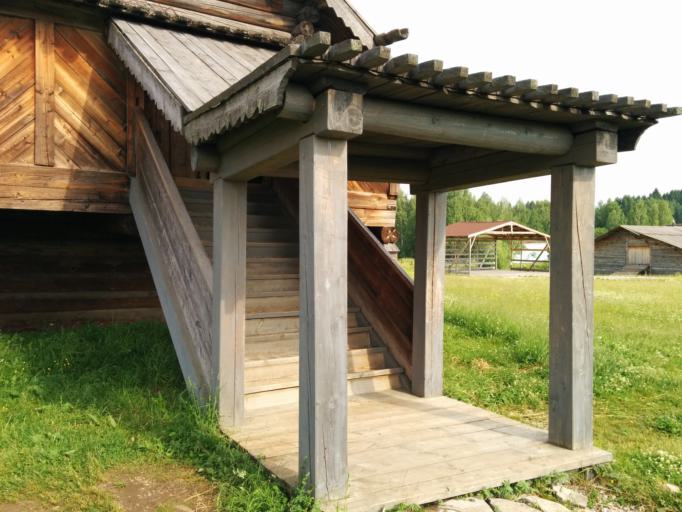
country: RU
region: Perm
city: Polazna
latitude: 58.2603
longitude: 56.2604
